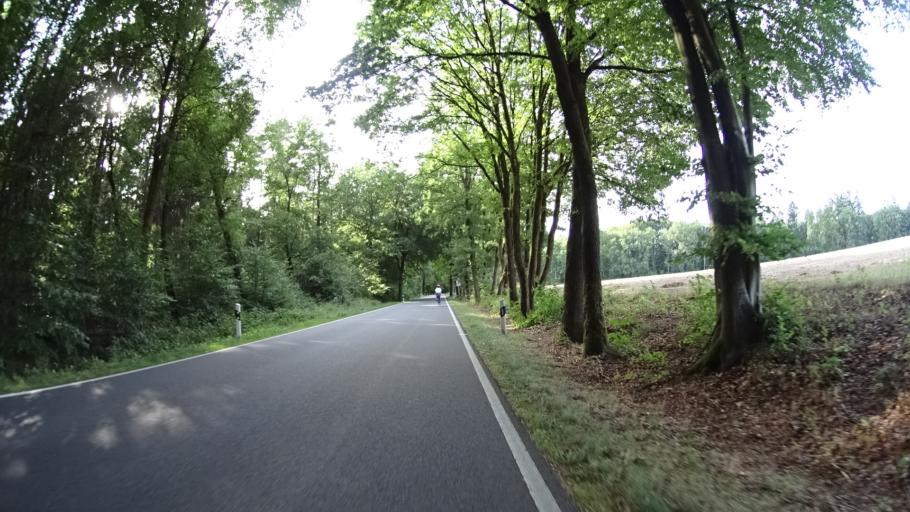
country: DE
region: Lower Saxony
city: Undeloh
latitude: 53.1623
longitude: 9.8988
